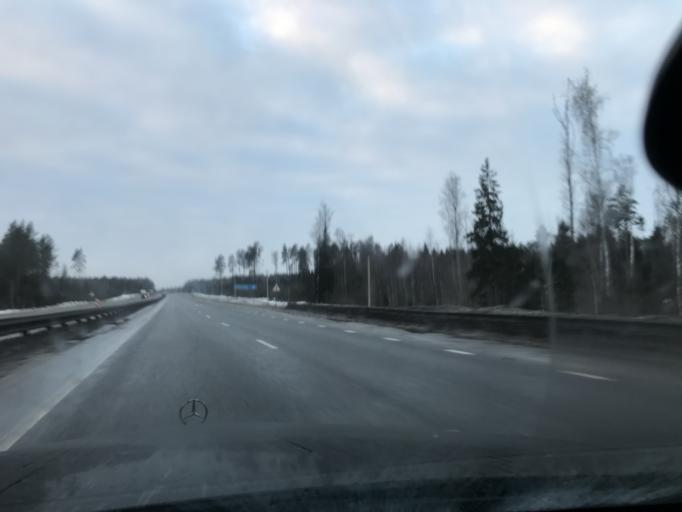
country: RU
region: Vladimir
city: Orgtrud
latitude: 56.1038
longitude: 40.6579
